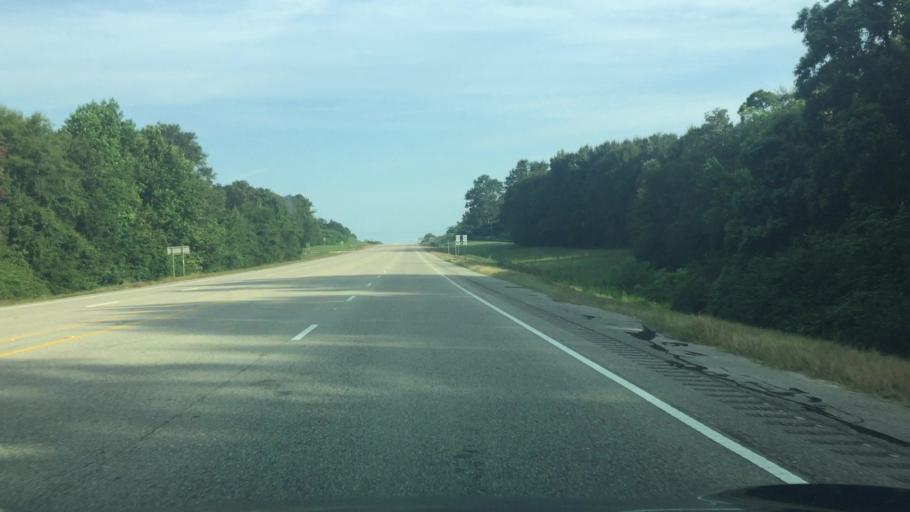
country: US
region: Alabama
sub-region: Butler County
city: Georgiana
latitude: 31.5358
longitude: -86.7248
